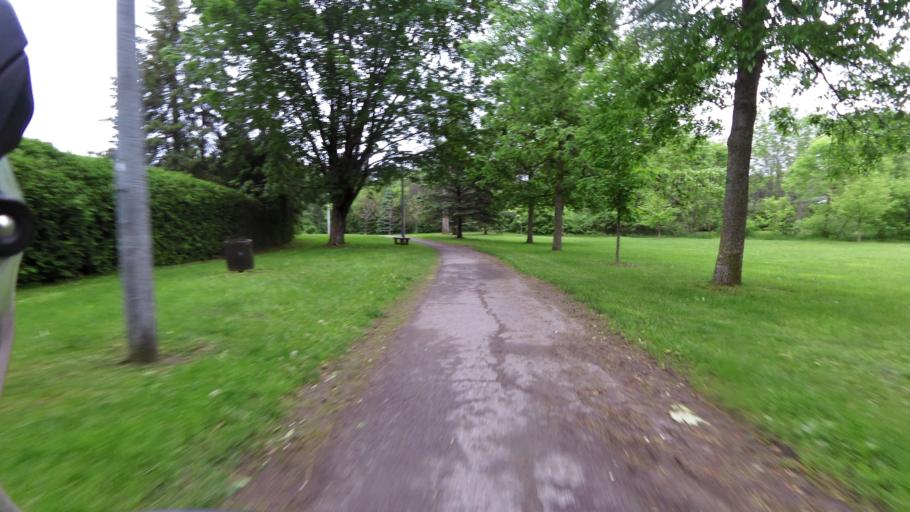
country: CA
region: Ontario
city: Bells Corners
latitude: 45.3118
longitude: -75.8883
